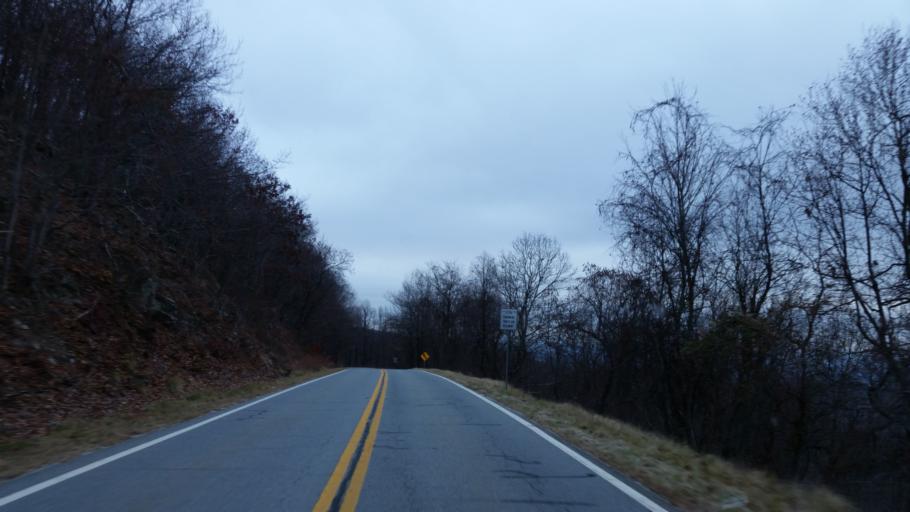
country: US
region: Georgia
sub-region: Pickens County
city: Jasper
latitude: 34.5411
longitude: -84.3419
